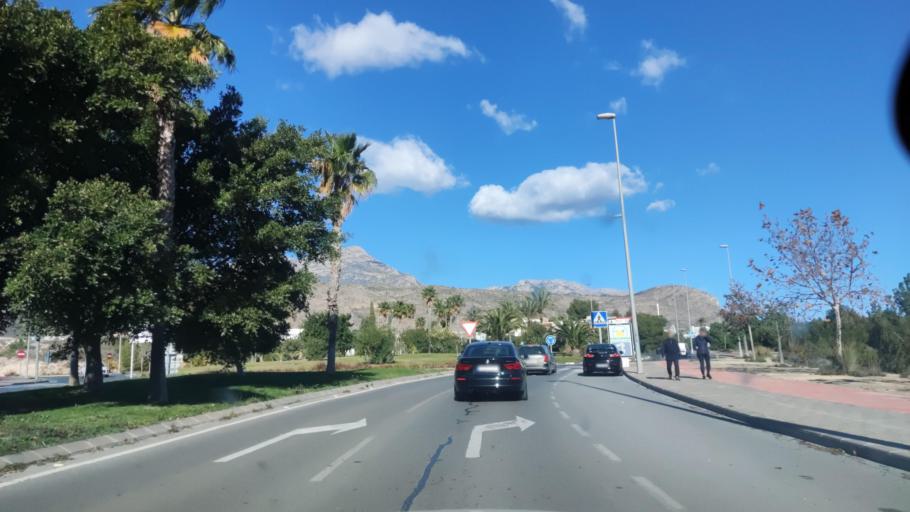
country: ES
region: Valencia
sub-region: Provincia de Alicante
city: Benidorm
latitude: 38.5423
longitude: -0.1599
